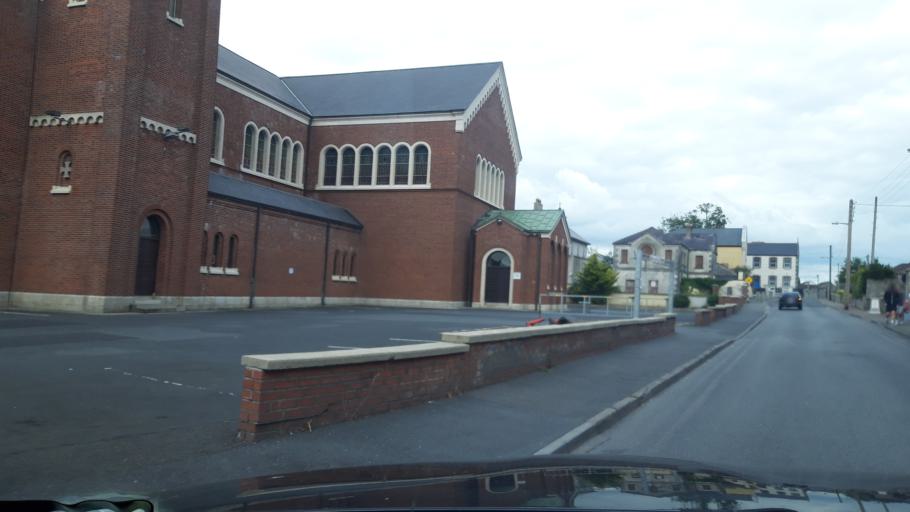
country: IE
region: Leinster
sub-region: Kildare
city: Athy
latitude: 52.9934
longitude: -6.9838
